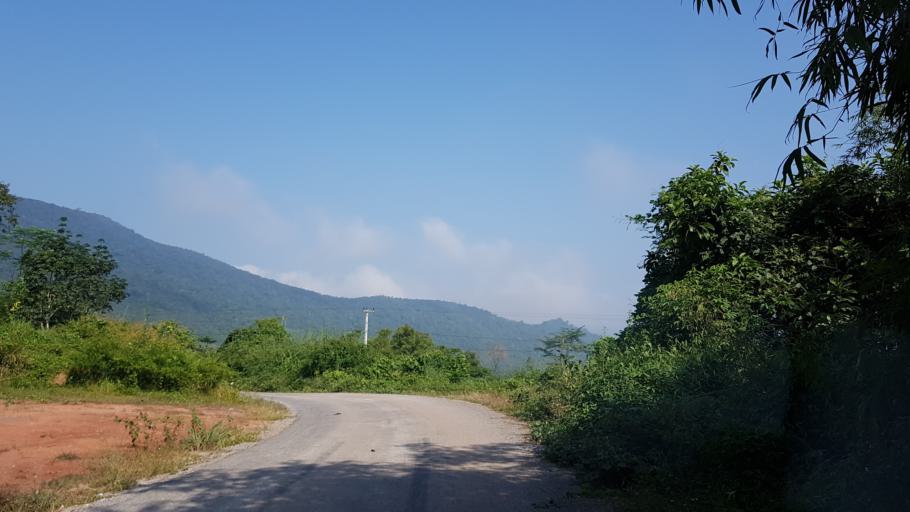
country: LA
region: Oudomxai
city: Muang Xay
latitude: 20.7150
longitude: 102.0898
